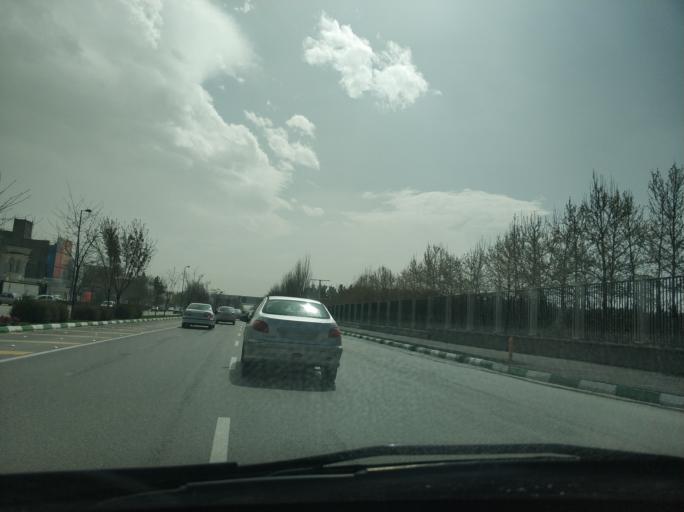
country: IR
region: Razavi Khorasan
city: Mashhad
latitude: 36.3122
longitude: 59.5449
